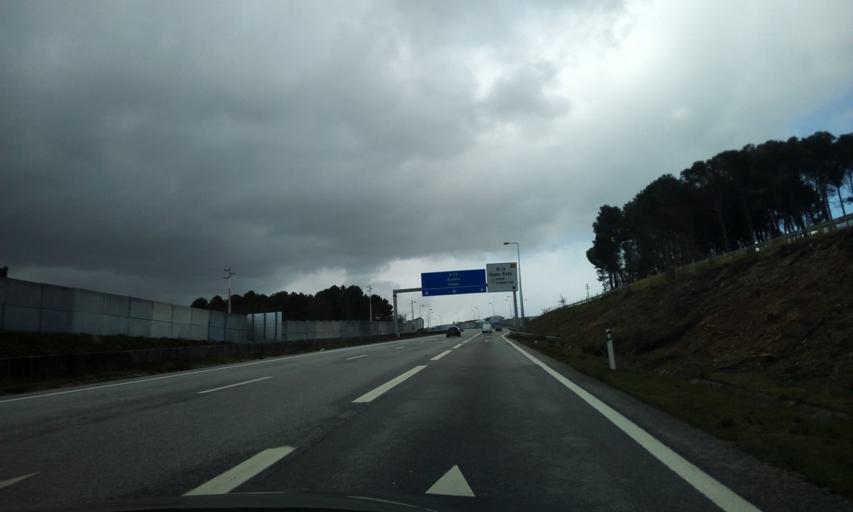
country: PT
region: Viseu
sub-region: Viseu
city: Rio de Loba
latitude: 40.6350
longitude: -7.8465
